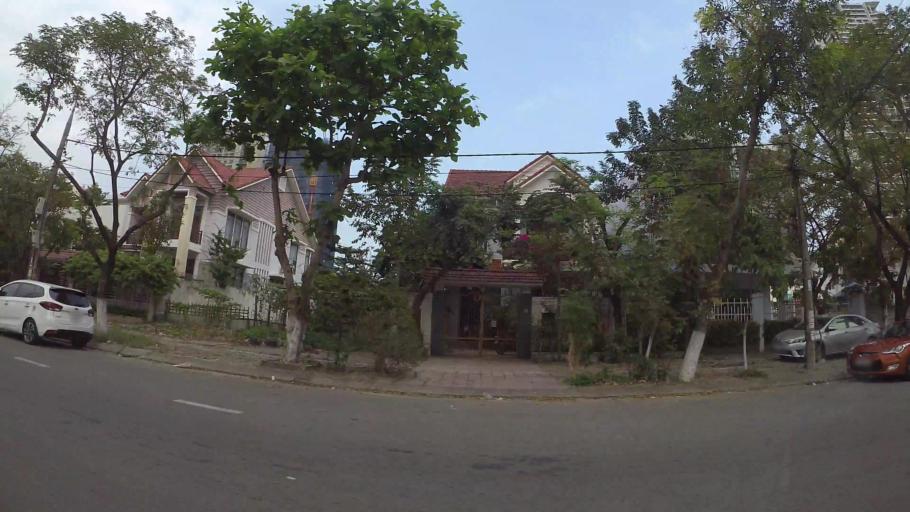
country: VN
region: Da Nang
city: Son Tra
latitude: 16.0730
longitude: 108.2430
